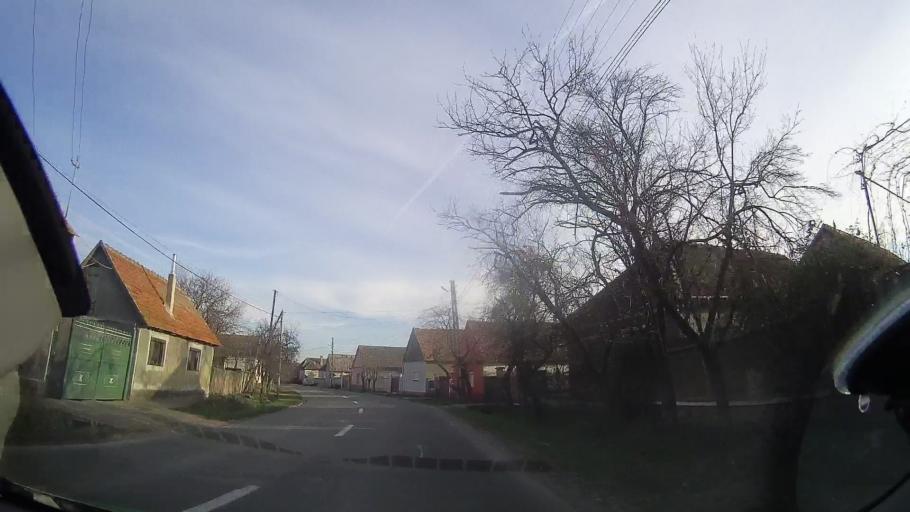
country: RO
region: Bihor
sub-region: Comuna Tileagd
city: Tileagd
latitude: 47.0630
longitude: 22.2328
